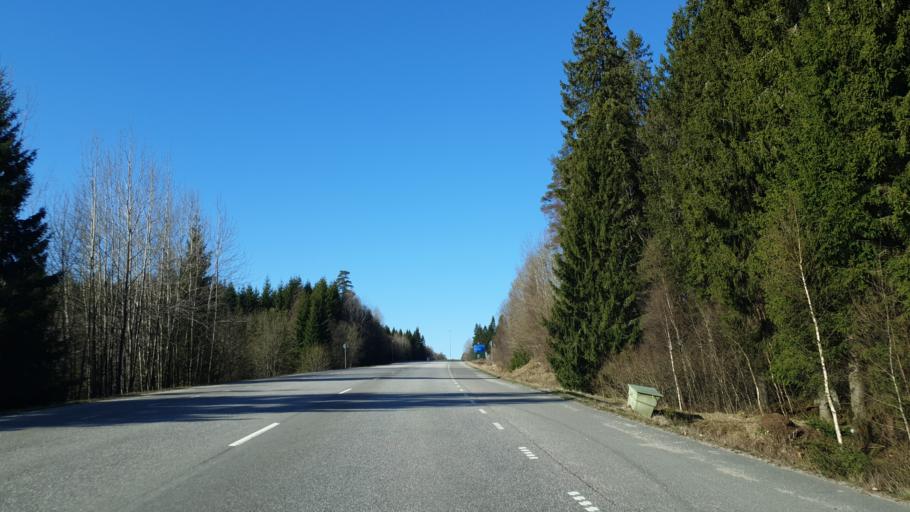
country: SE
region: Vaestra Goetaland
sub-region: Boras Kommun
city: Dalsjofors
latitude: 57.7586
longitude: 13.1085
